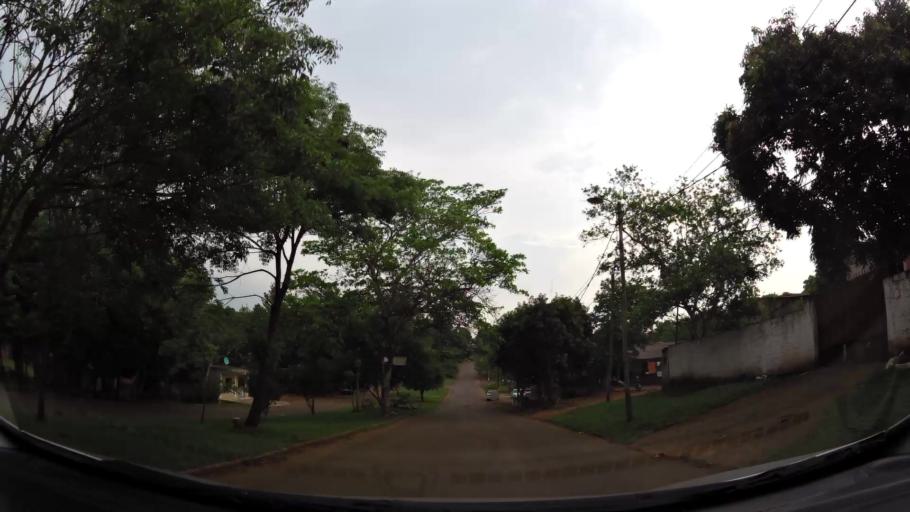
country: BR
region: Parana
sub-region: Foz Do Iguacu
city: Foz do Iguacu
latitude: -25.5458
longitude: -54.5981
